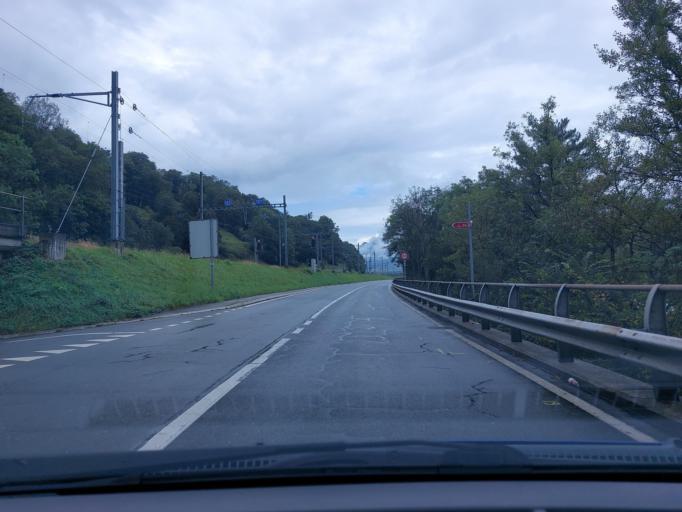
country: CH
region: Valais
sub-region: Saint-Maurice District
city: Saint-Maurice
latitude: 46.2251
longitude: 7.0019
